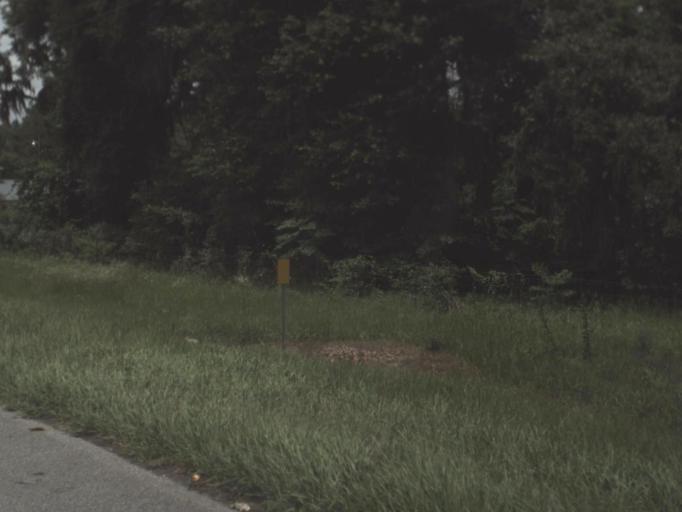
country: US
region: Florida
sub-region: Madison County
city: Madison
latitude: 30.6336
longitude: -83.4413
